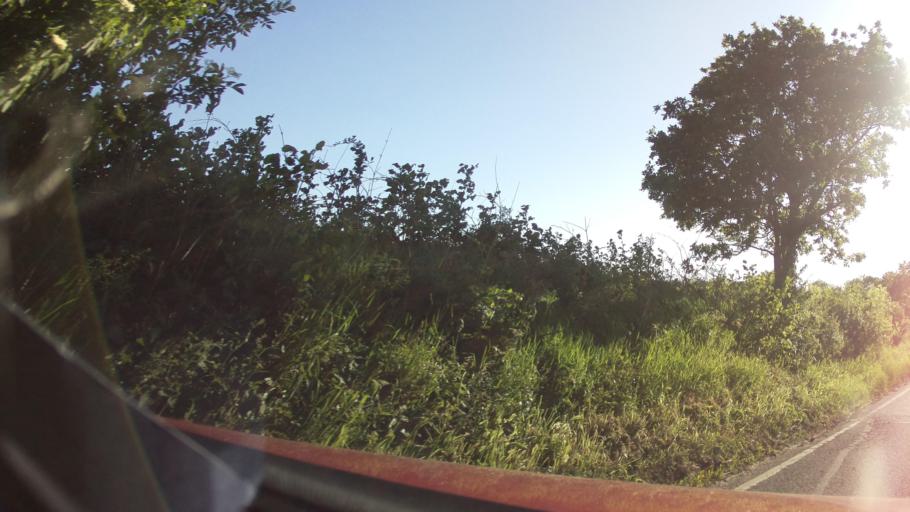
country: GB
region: England
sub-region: Devon
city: Sidmouth
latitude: 50.7158
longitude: -3.1582
